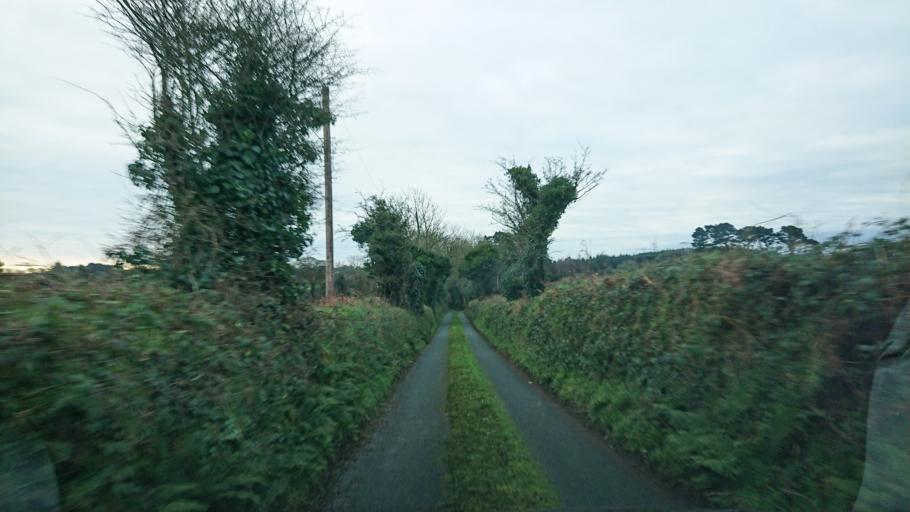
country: IE
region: Leinster
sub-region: Kilkenny
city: Mooncoin
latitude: 52.2183
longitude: -7.2713
